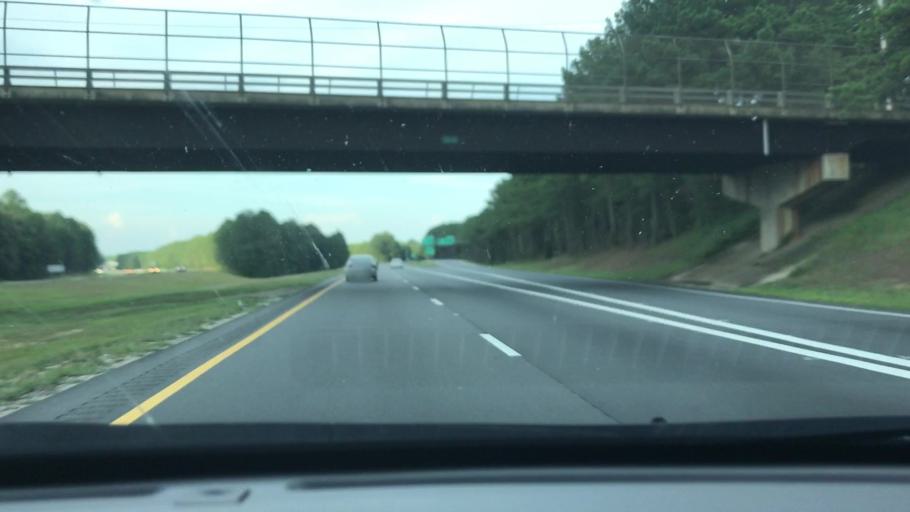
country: US
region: North Carolina
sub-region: Cumberland County
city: Hope Mills
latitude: 34.9725
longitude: -78.8652
